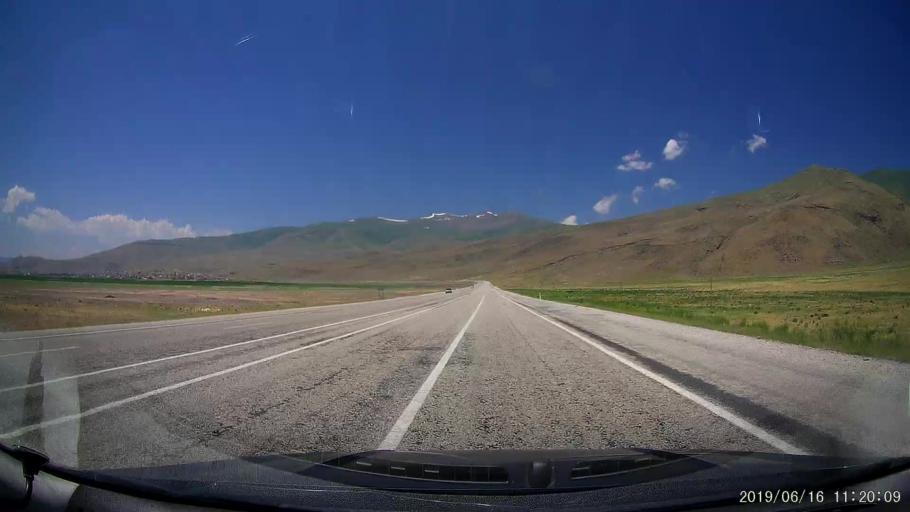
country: TR
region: Agri
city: Dogubayazit
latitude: 39.6974
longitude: 44.0976
